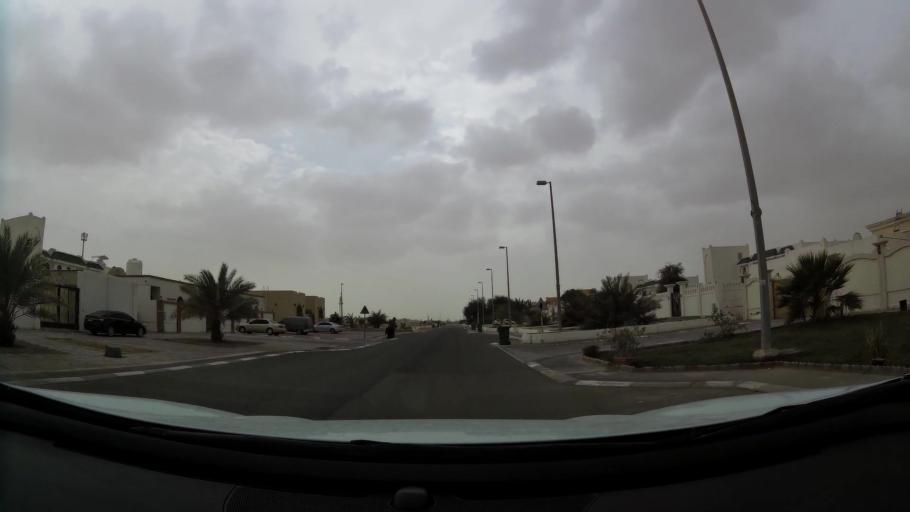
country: AE
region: Abu Dhabi
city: Abu Dhabi
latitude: 24.3689
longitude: 54.6652
